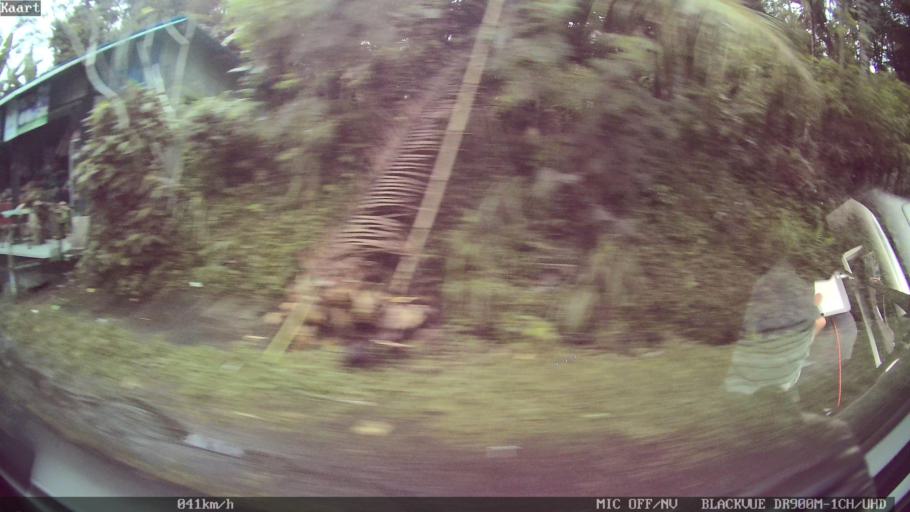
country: ID
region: Bali
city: Pegongan
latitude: -8.4811
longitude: 115.2281
